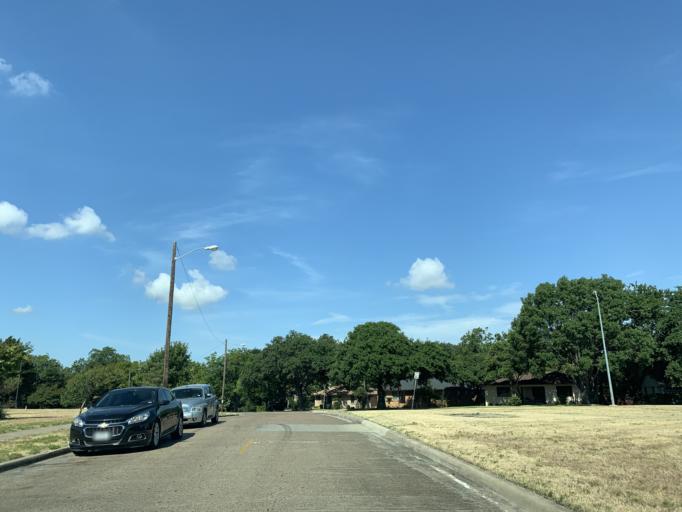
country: US
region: Texas
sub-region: Dallas County
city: Cockrell Hill
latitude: 32.7443
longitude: -96.8621
